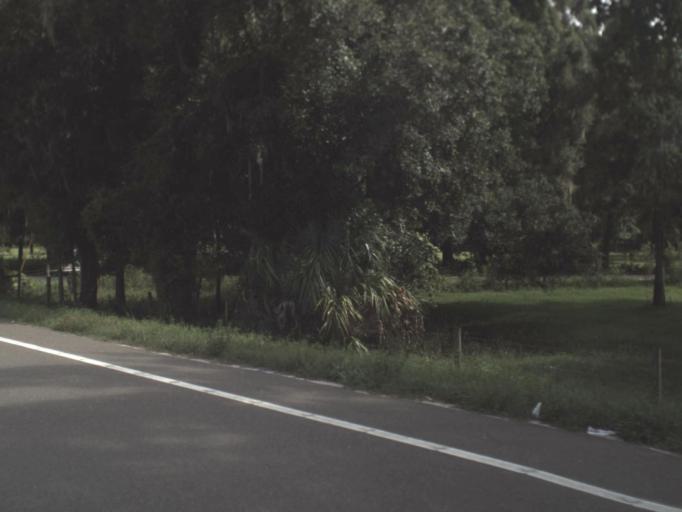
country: US
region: Florida
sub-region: Pasco County
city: Crystal Springs
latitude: 28.1896
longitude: -82.1620
